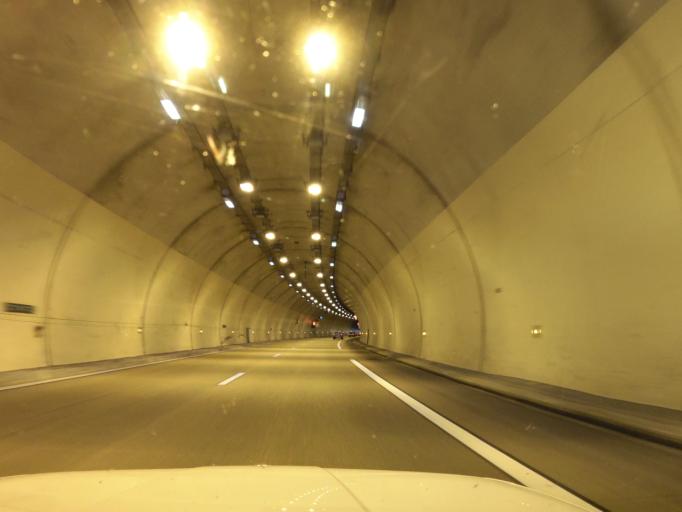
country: FR
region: Languedoc-Roussillon
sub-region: Departement de l'Herault
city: Lodeve
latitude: 43.7291
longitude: 3.3269
